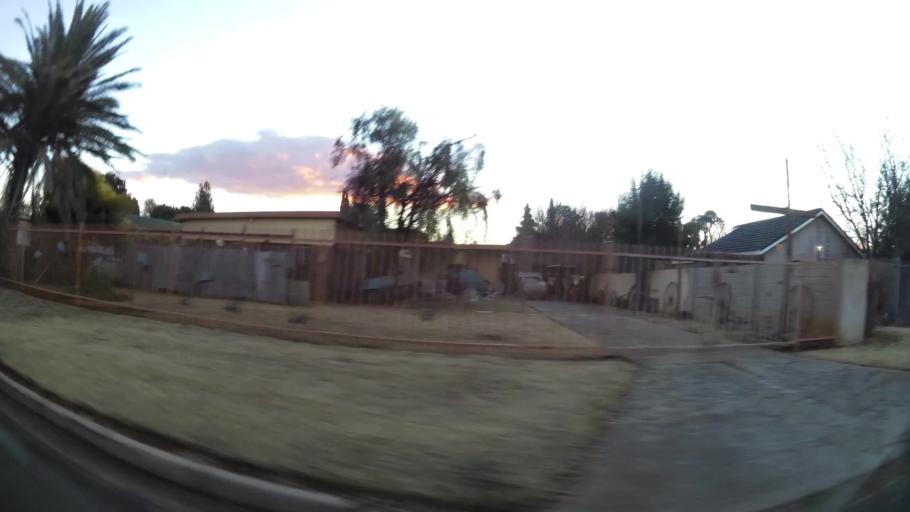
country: ZA
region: North-West
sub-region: Dr Kenneth Kaunda District Municipality
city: Potchefstroom
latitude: -26.7124
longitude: 27.1161
